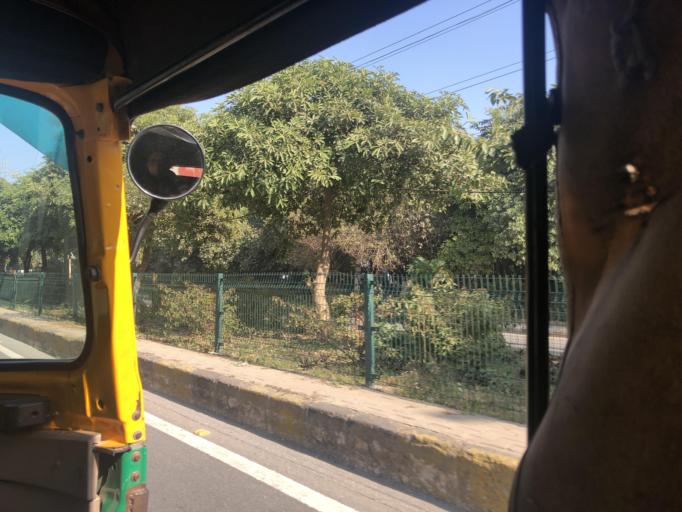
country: IN
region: Haryana
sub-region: Gurgaon
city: Gurgaon
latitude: 28.4328
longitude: 77.0908
